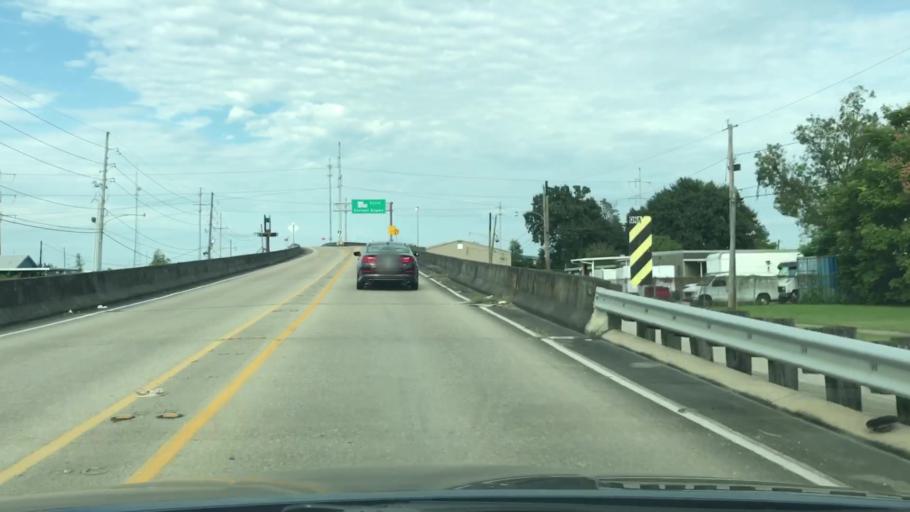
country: US
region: Louisiana
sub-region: Jefferson Parish
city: Jefferson
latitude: 29.9673
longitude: -90.1461
